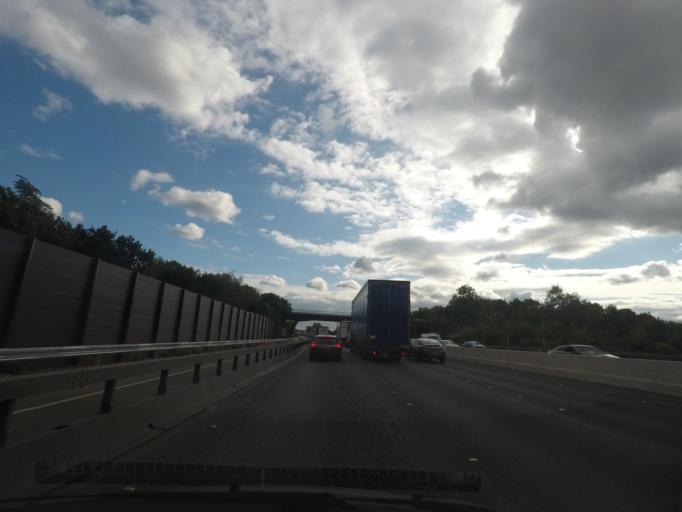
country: GB
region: England
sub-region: Derbyshire
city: Long Eaton
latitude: 52.8822
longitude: -1.3098
